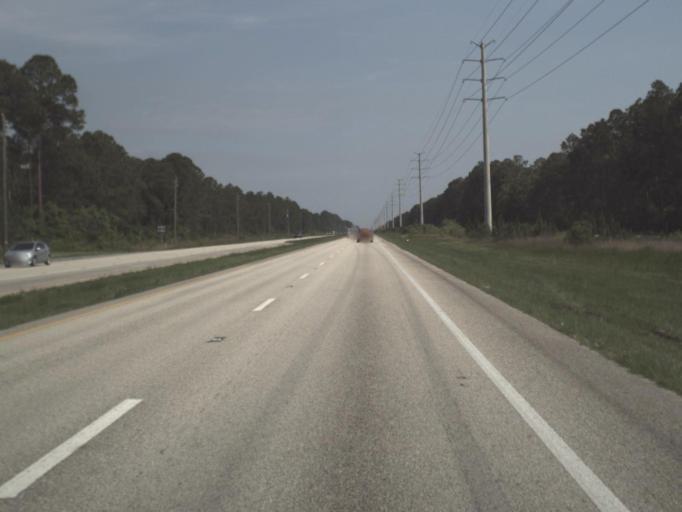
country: US
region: Florida
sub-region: Saint Johns County
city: Villano Beach
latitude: 30.0283
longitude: -81.4064
